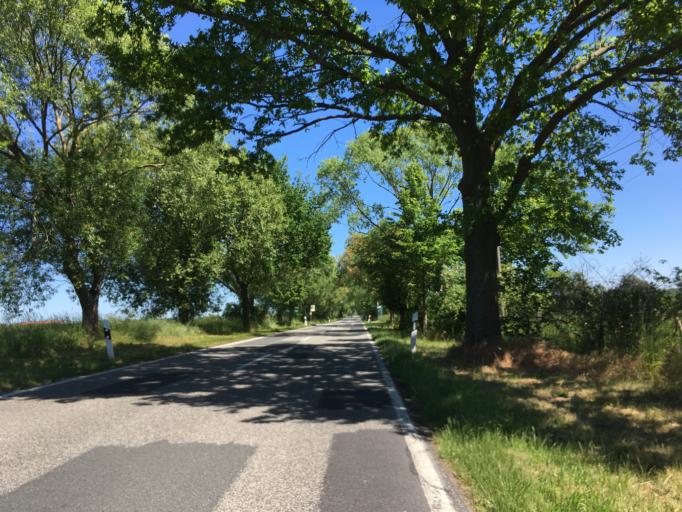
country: DE
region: Brandenburg
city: Zehdenick
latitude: 52.9452
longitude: 13.2769
